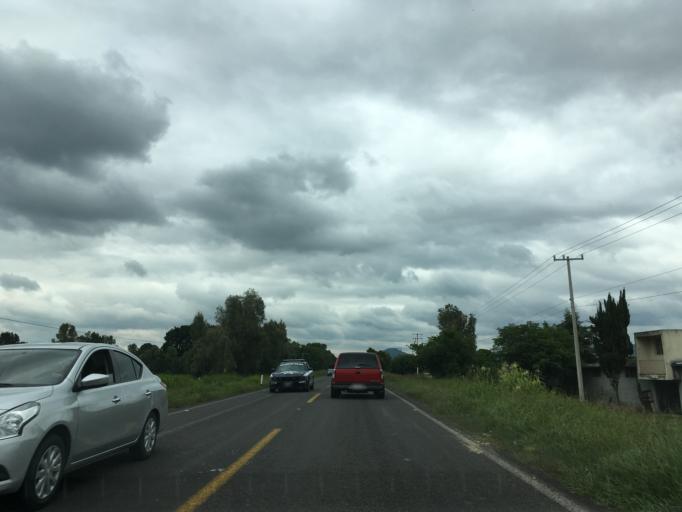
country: MX
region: Michoacan
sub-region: Cuitzeo
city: Cuamio
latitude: 20.0205
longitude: -101.1539
